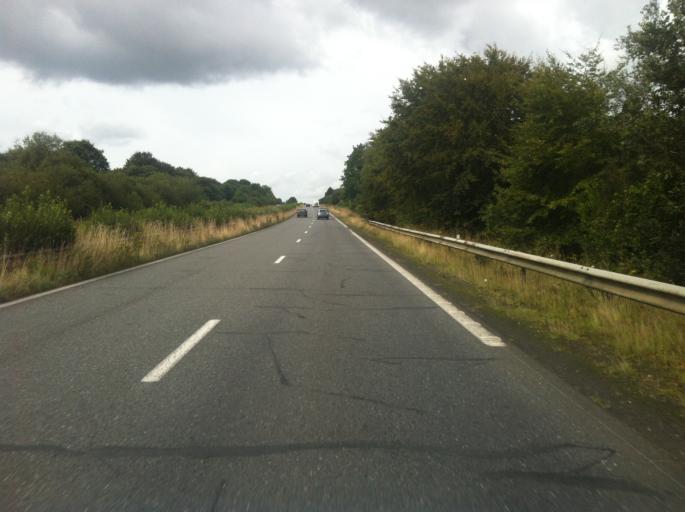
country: FR
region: Brittany
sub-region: Departement du Finistere
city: La Roche-Maurice
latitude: 48.4925
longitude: -4.2178
